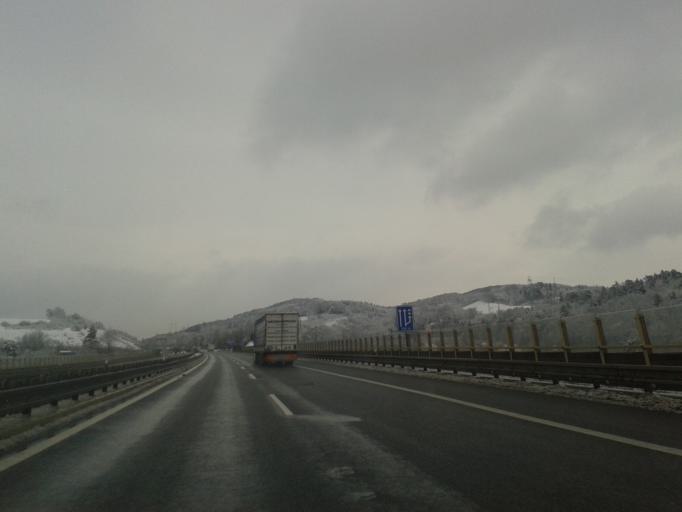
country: CZ
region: Central Bohemia
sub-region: Okres Beroun
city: Beroun
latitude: 49.9628
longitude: 14.0872
